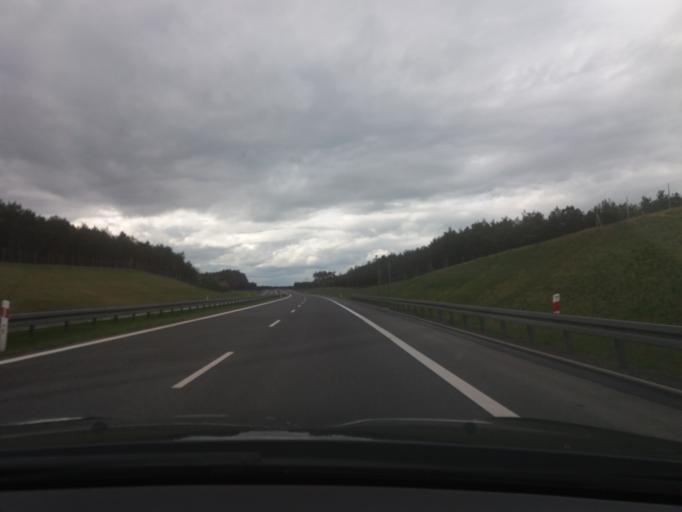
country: PL
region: Lubusz
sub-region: Powiat miedzyrzecki
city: Bledzew
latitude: 52.6114
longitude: 15.4095
